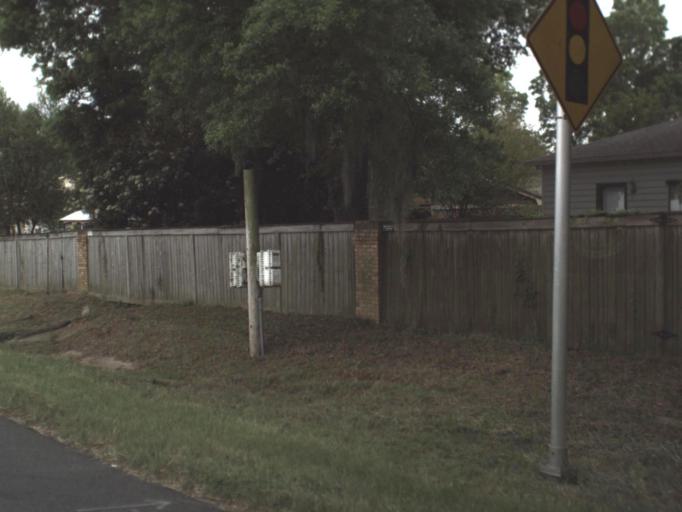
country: US
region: Florida
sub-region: Escambia County
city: Ferry Pass
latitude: 30.5180
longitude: -87.1685
